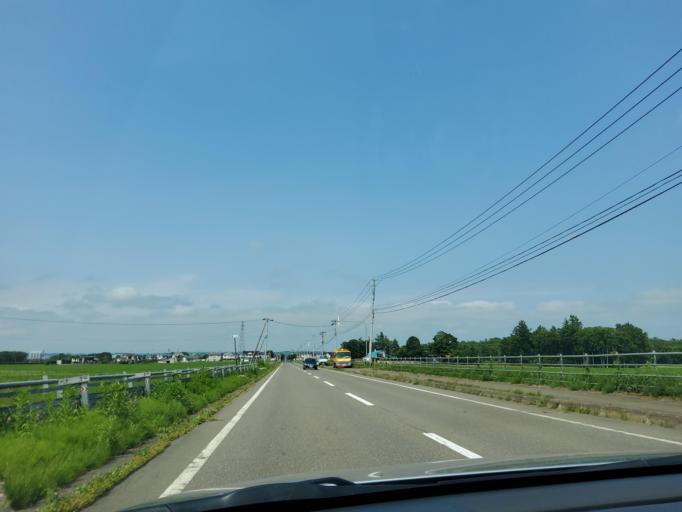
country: JP
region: Hokkaido
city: Obihiro
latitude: 42.8944
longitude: 143.0424
